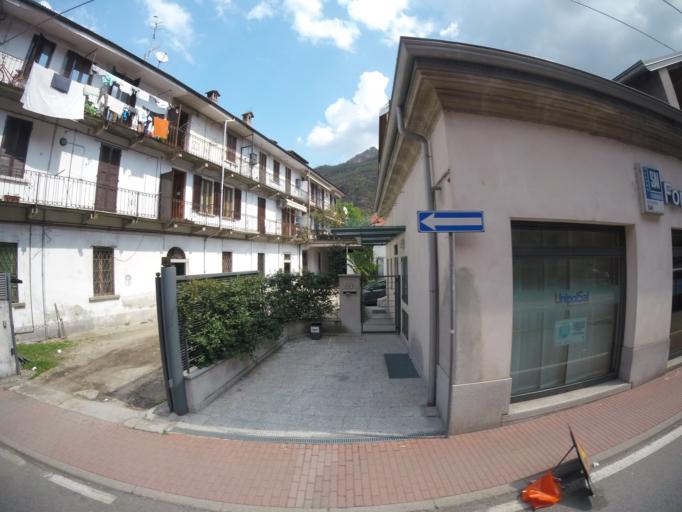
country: IT
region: Piedmont
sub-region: Provincia Verbano-Cusio-Ossola
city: Omegna
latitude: 45.8743
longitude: 8.4115
